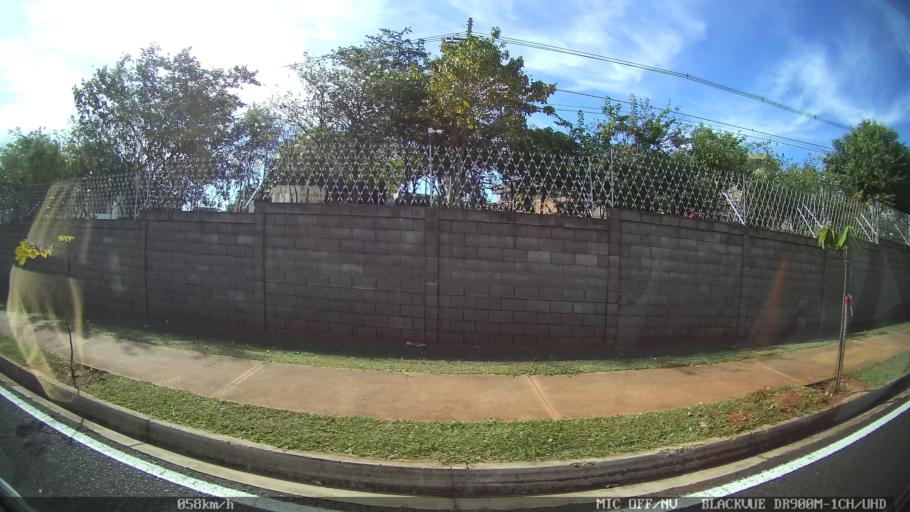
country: BR
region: Sao Paulo
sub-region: Sao Jose Do Rio Preto
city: Sao Jose do Rio Preto
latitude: -20.8097
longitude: -49.3401
